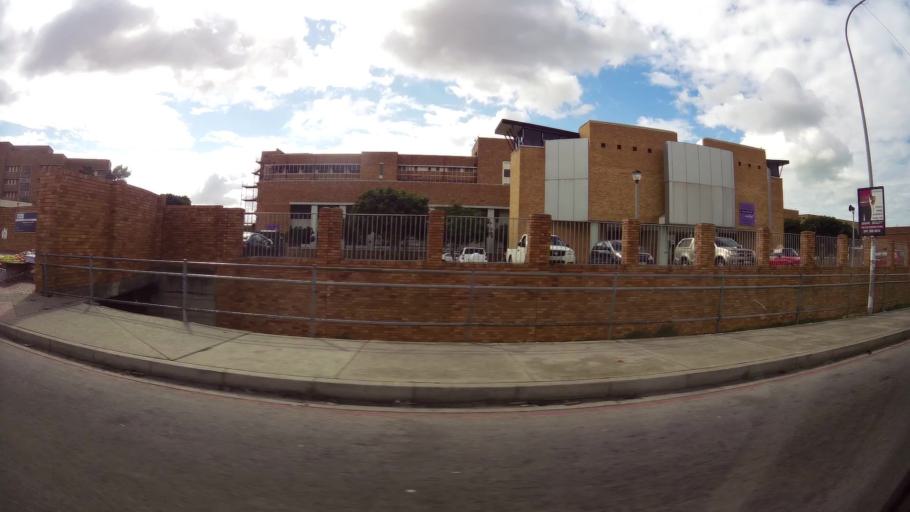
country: ZA
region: Eastern Cape
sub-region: Nelson Mandela Bay Metropolitan Municipality
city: Port Elizabeth
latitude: -33.9256
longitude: 25.5700
